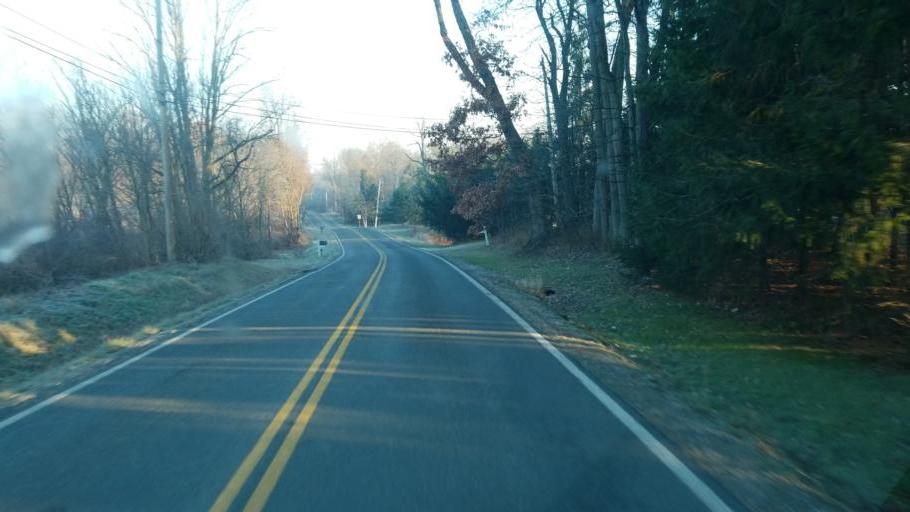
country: US
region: Ohio
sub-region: Medina County
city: Medina
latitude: 41.0939
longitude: -81.8038
